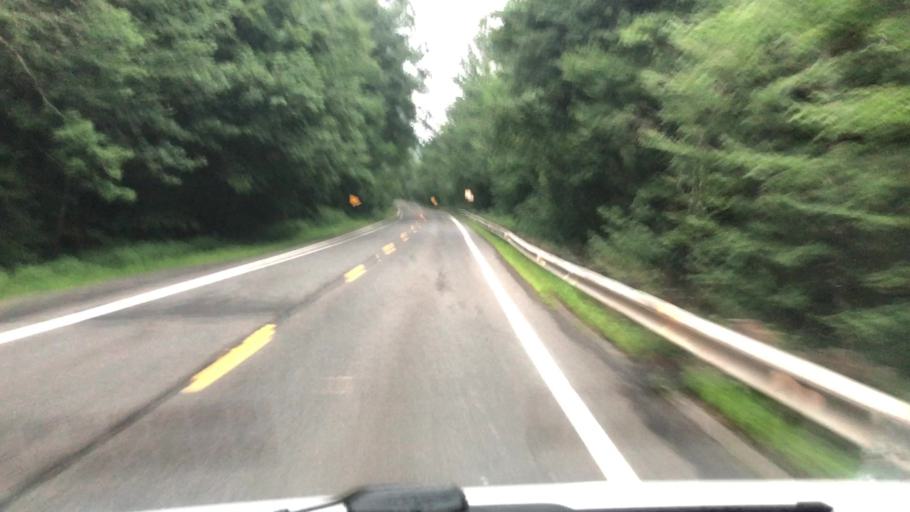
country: US
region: Massachusetts
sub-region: Hampshire County
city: Chesterfield
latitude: 42.3107
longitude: -72.8637
